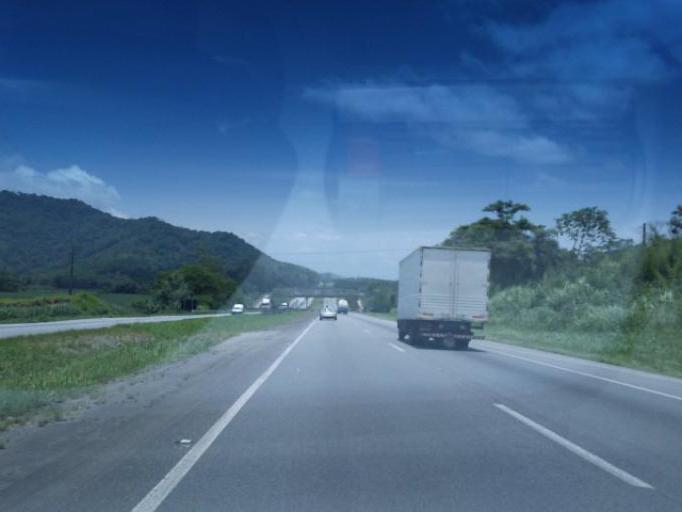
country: BR
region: Sao Paulo
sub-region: Miracatu
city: Miracatu
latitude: -24.3106
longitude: -47.5106
